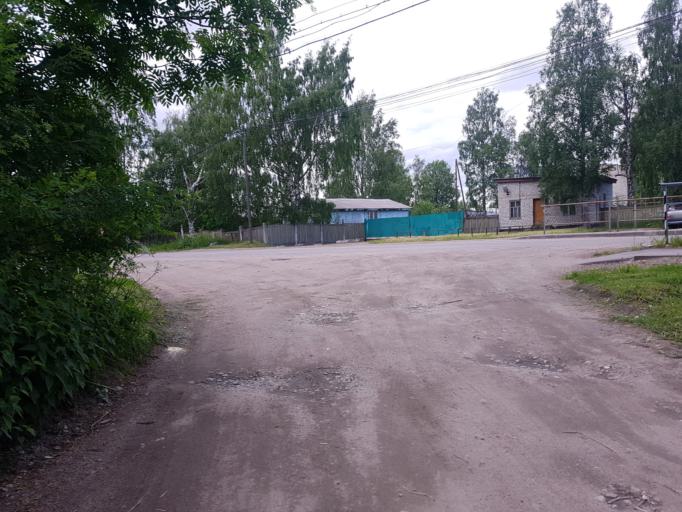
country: RU
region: Republic of Karelia
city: Kalevala
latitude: 65.1962
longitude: 31.1992
